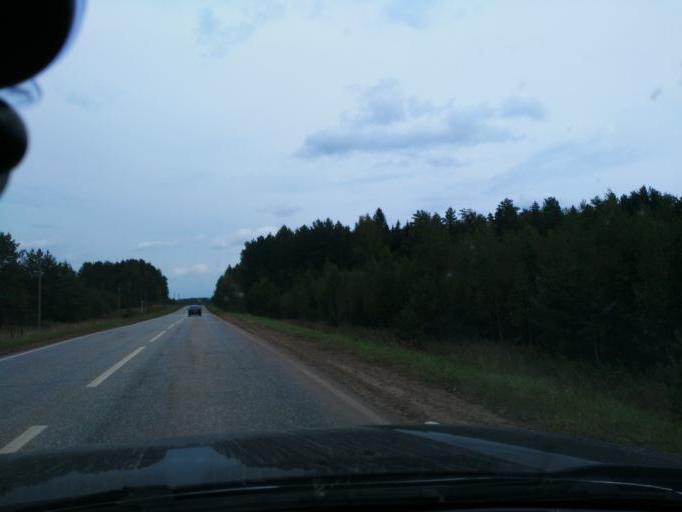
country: RU
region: Perm
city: Kuyeda
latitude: 56.4751
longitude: 55.7583
